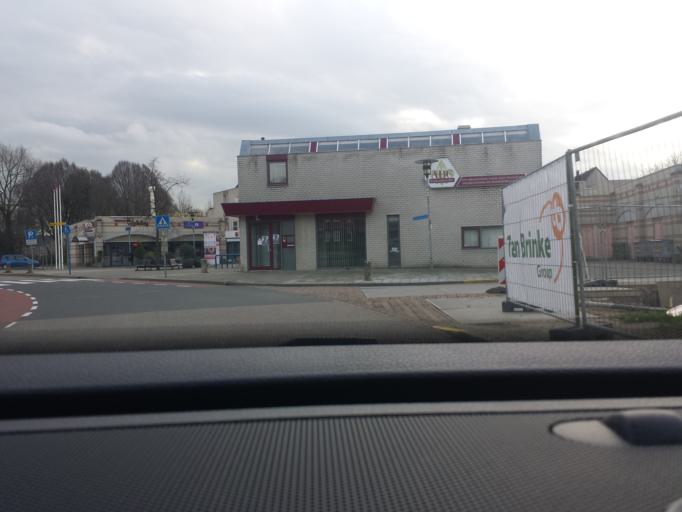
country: NL
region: Gelderland
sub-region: Gemeente Duiven
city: Duiven
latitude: 51.9487
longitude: 6.0237
